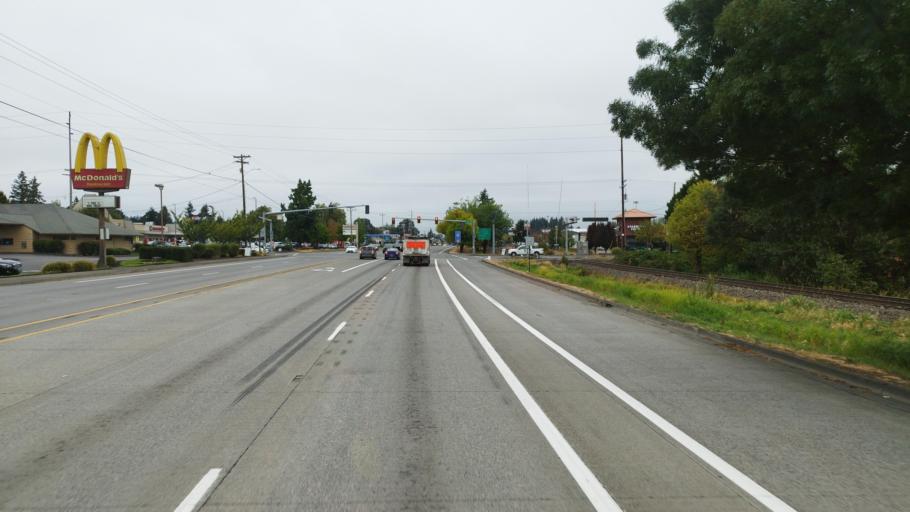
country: US
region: Oregon
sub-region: Columbia County
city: Saint Helens
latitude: 45.8478
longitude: -122.8323
